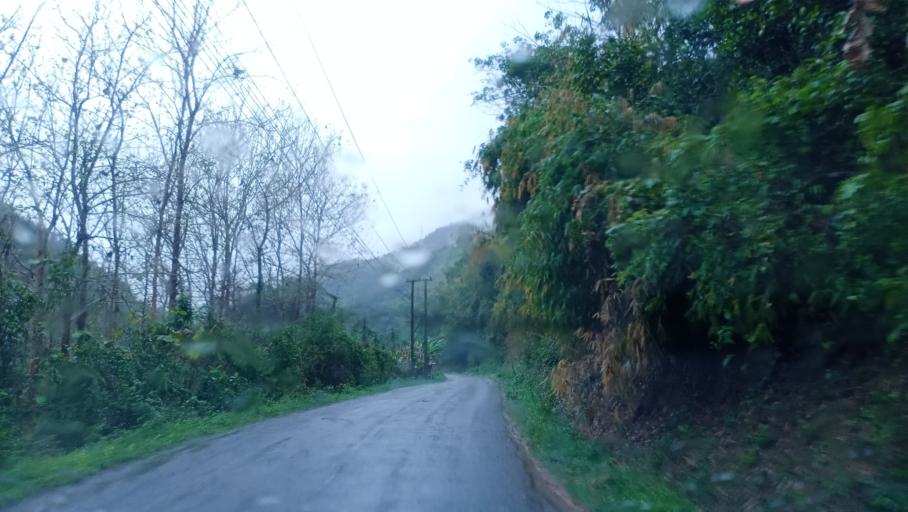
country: LA
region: Phongsali
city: Khoa
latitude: 21.0618
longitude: 102.4724
